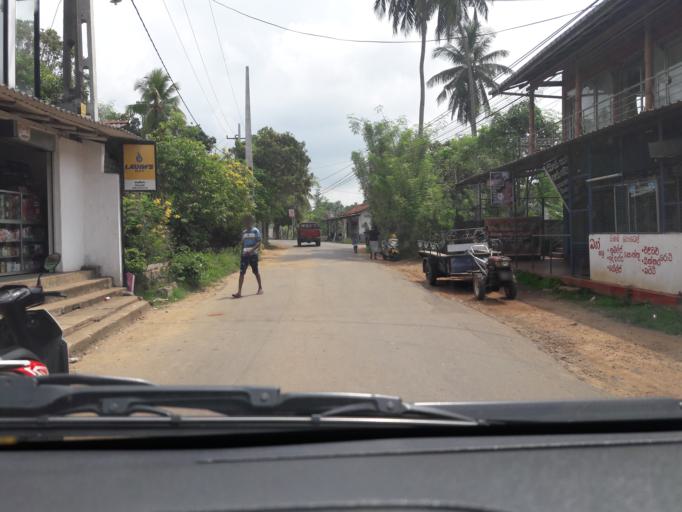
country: LK
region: Southern
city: Hikkaduwa
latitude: 6.0965
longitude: 80.1523
